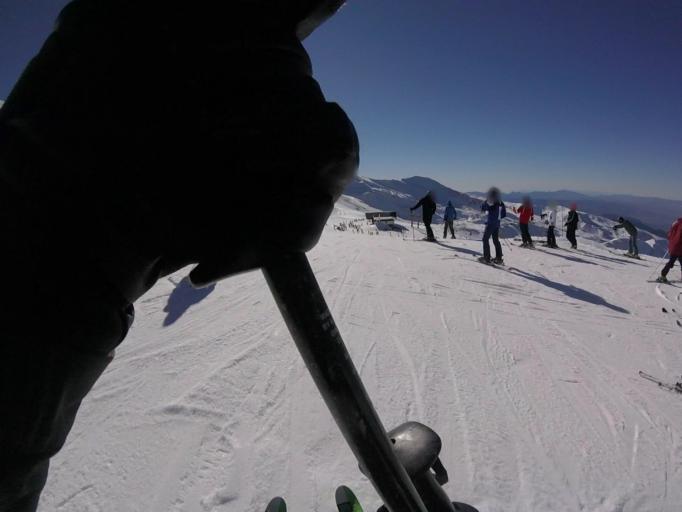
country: ES
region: Andalusia
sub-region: Provincia de Granada
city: Capileira
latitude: 37.0637
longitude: -3.3725
